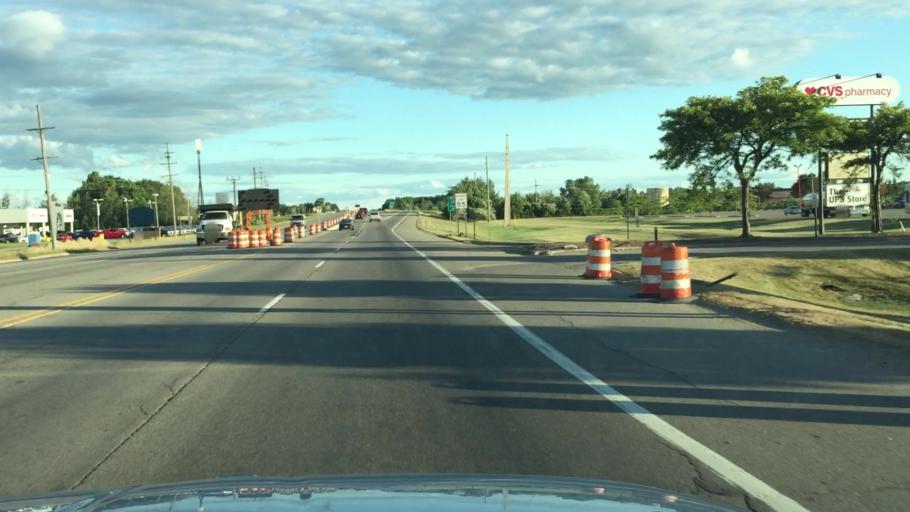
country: US
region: Michigan
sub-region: Lapeer County
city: Imlay City
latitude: 43.0064
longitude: -83.0716
